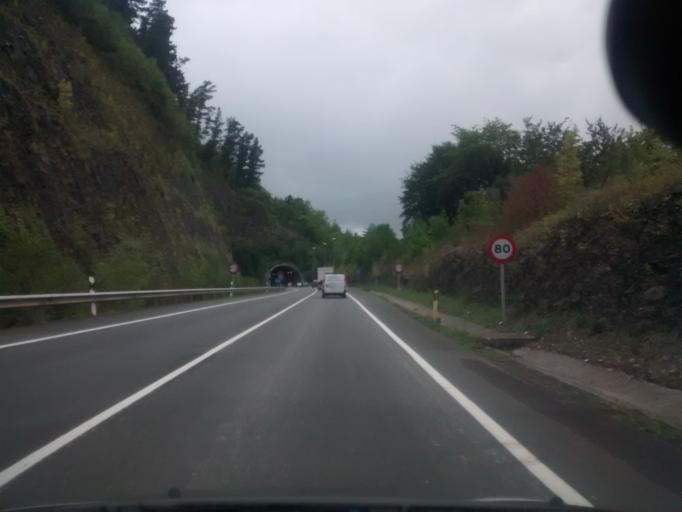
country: ES
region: Basque Country
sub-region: Provincia de Guipuzcoa
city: Bergara
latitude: 43.1078
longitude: -2.4076
